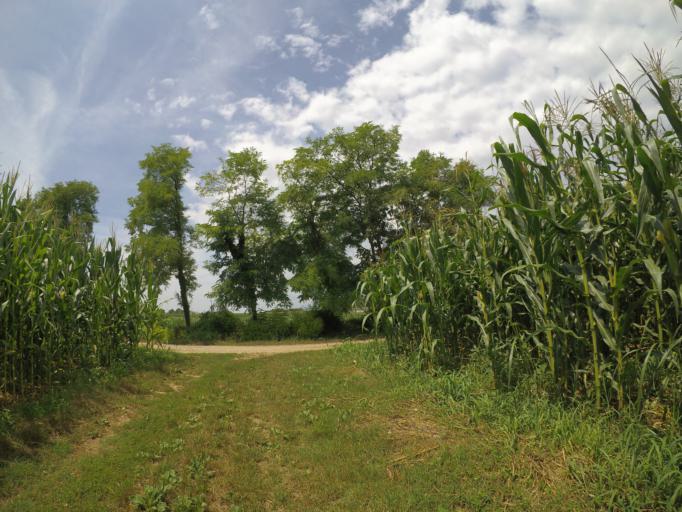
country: IT
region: Friuli Venezia Giulia
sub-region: Provincia di Udine
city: Bertiolo
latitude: 45.9683
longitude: 13.0642
